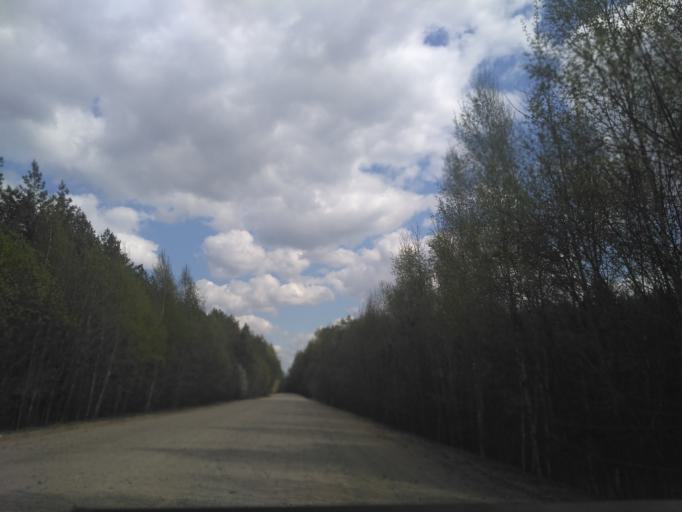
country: BY
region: Minsk
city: Radashkovichy
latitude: 54.2649
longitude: 27.3018
